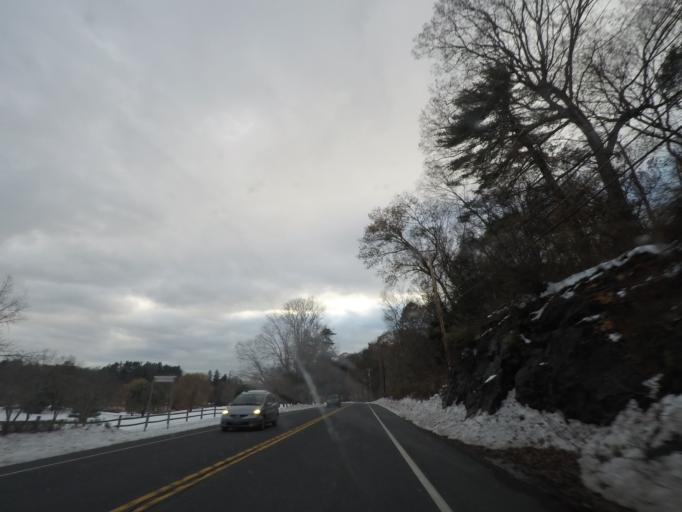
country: US
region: New York
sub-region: Ulster County
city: Rosendale Village
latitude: 41.8785
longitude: -74.0506
